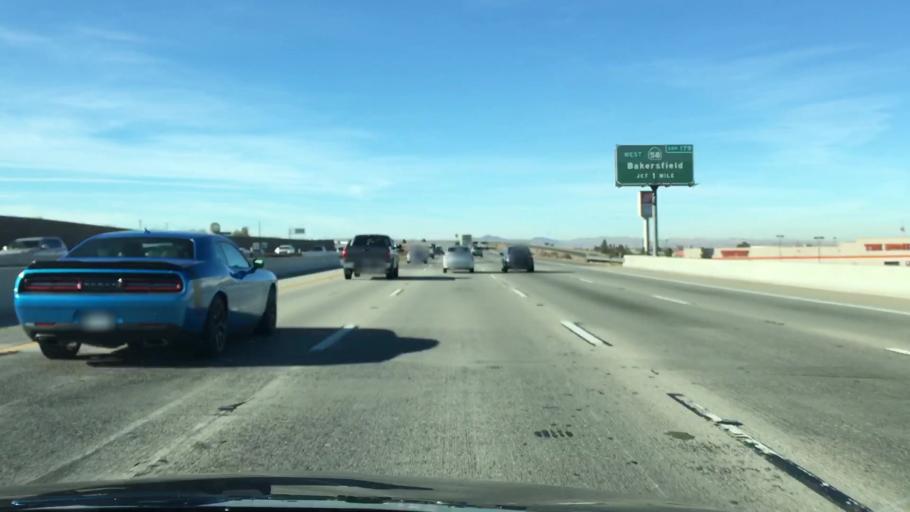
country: US
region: California
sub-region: San Bernardino County
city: Barstow Heights
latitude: 34.8849
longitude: -117.0562
